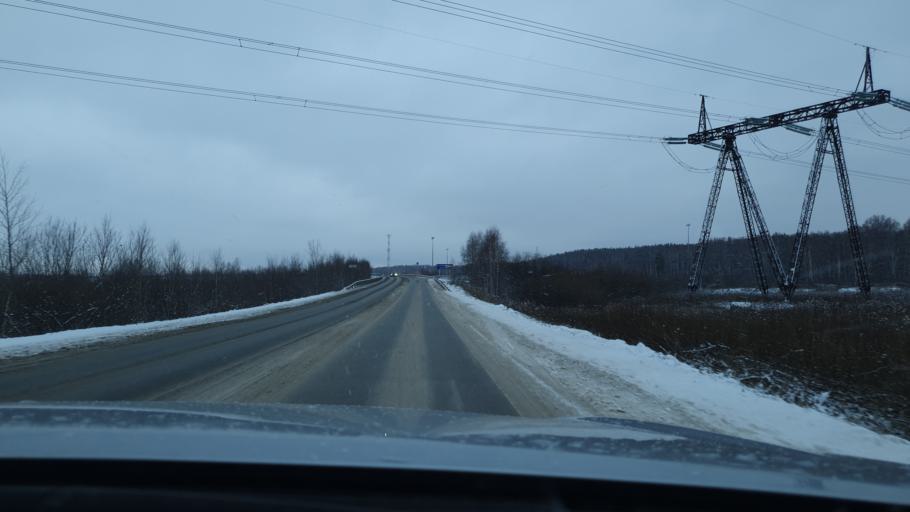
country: RU
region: Sverdlovsk
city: Istok
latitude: 56.7730
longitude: 60.7379
